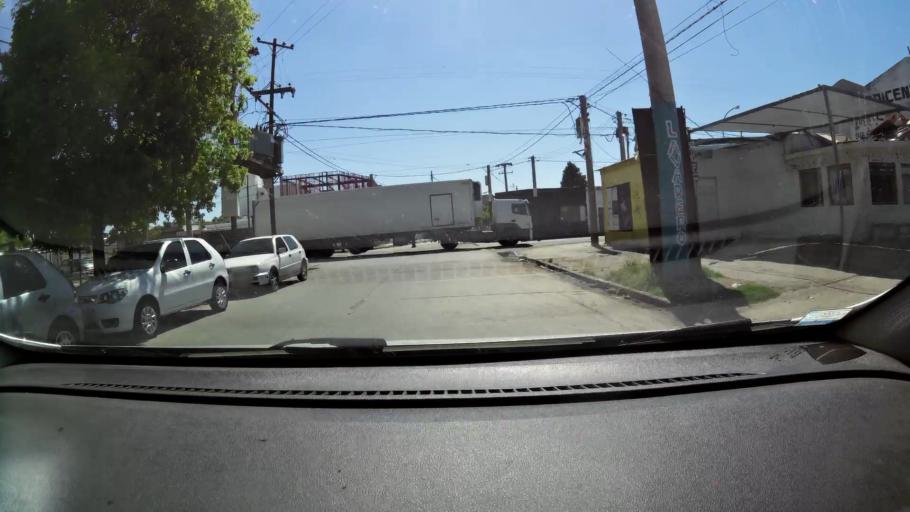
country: AR
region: Cordoba
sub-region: Departamento de Capital
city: Cordoba
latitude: -31.3755
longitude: -64.1476
